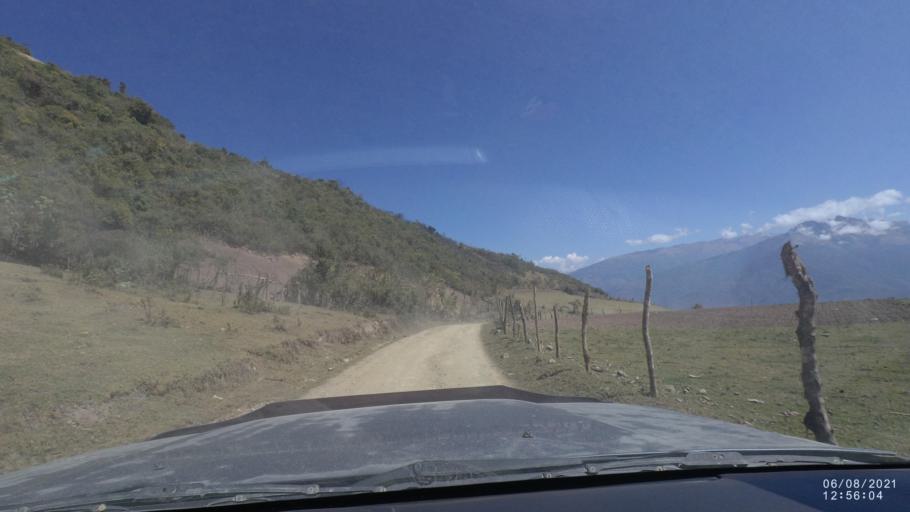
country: BO
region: Cochabamba
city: Colchani
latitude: -16.7564
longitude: -66.6854
